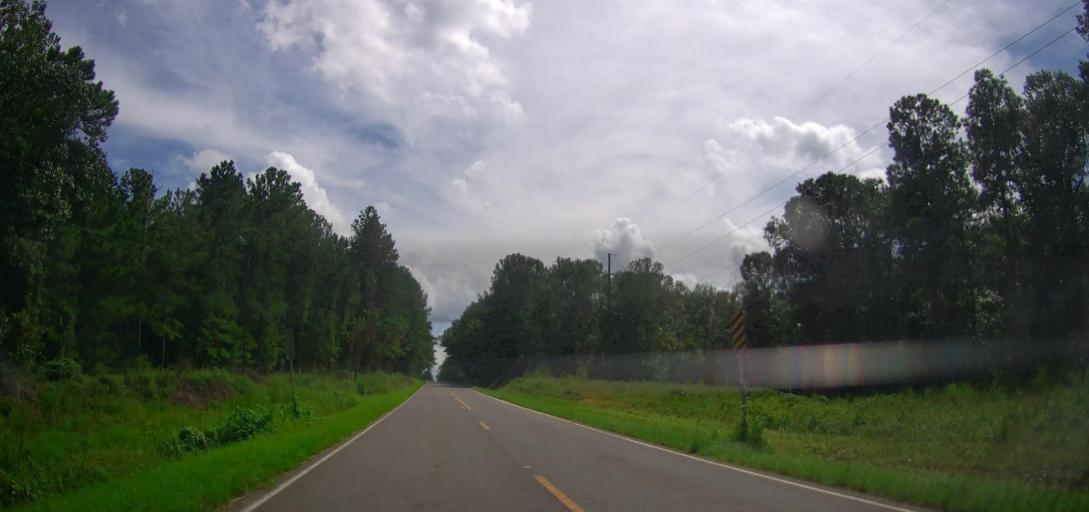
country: US
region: Georgia
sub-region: Taylor County
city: Butler
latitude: 32.5104
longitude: -84.2039
